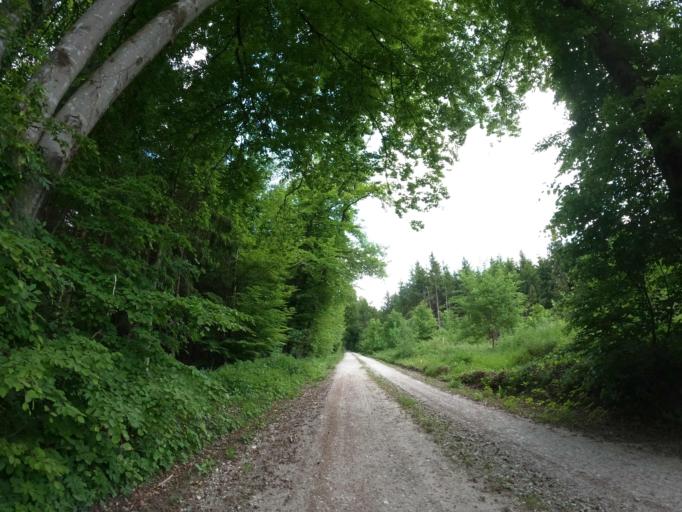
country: DE
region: Bavaria
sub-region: Upper Bavaria
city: Brunnthal
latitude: 47.9724
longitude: 11.7079
